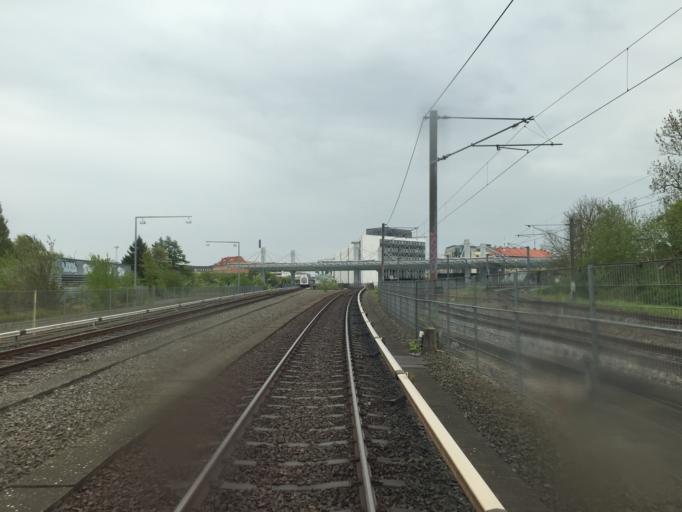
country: DK
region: Capital Region
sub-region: Kobenhavn
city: Vanlose
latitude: 55.6865
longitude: 12.4958
